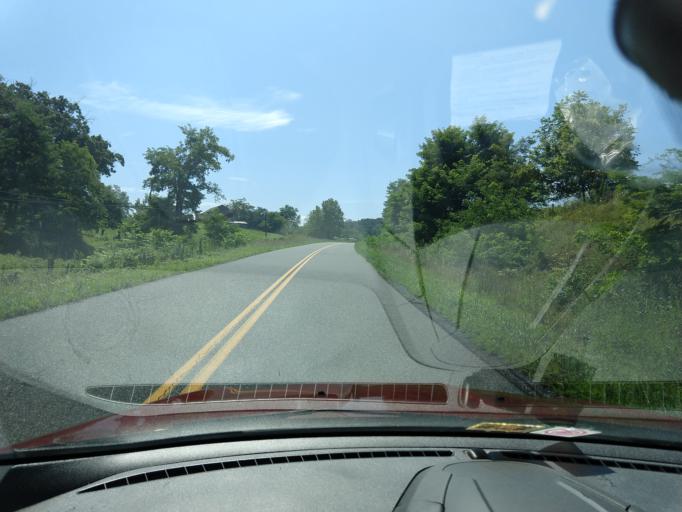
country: US
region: Virginia
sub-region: City of Harrisonburg
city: Harrisonburg
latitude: 38.5471
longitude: -78.8975
